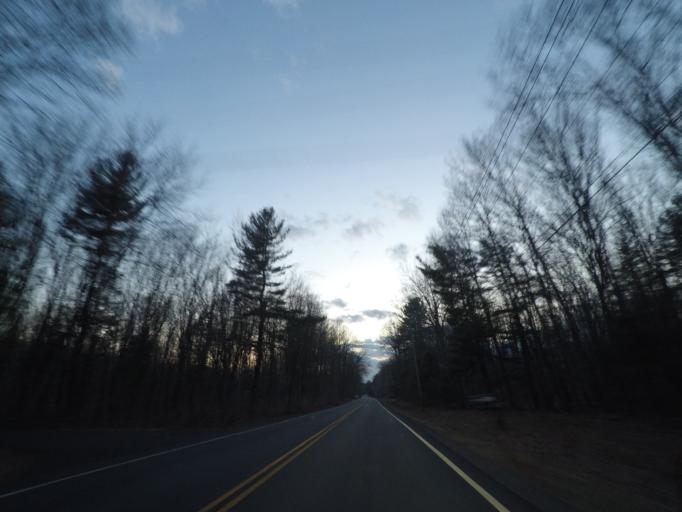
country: US
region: New York
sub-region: Schenectady County
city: Niskayuna
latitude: 42.8328
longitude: -73.7990
